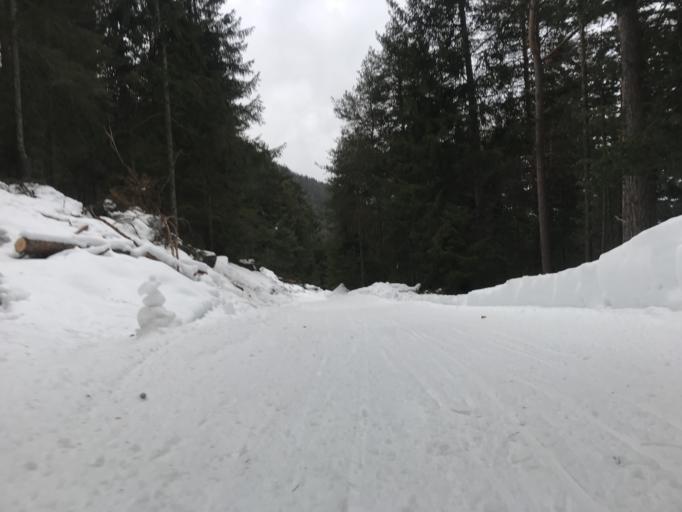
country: IT
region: Trentino-Alto Adige
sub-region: Bolzano
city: Funes - Villnoess
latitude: 46.6808
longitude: 11.6846
